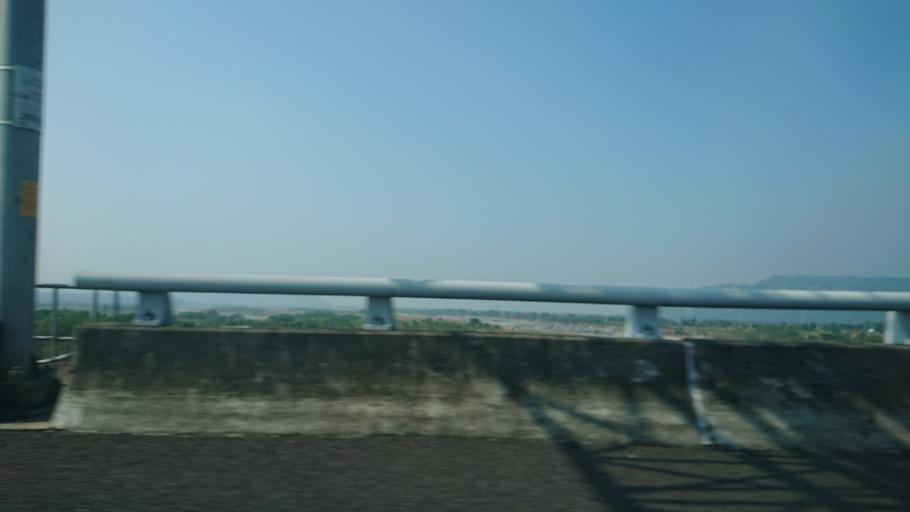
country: TW
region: Taiwan
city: Lugu
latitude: 23.8039
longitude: 120.6980
